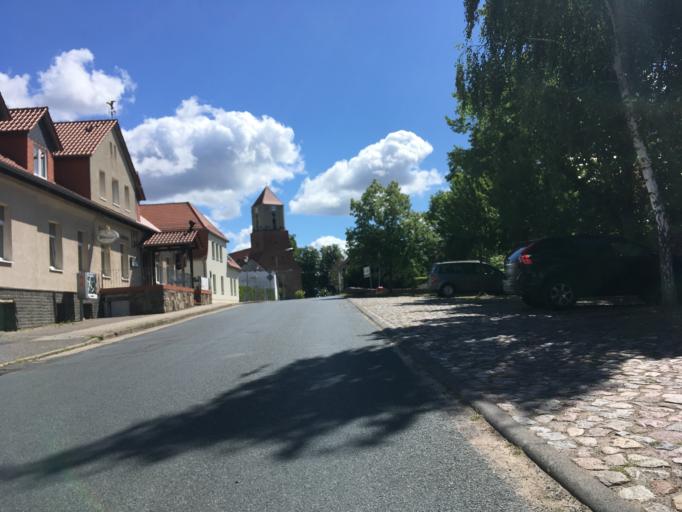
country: DE
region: Brandenburg
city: Gerswalde
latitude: 53.1707
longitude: 13.7484
